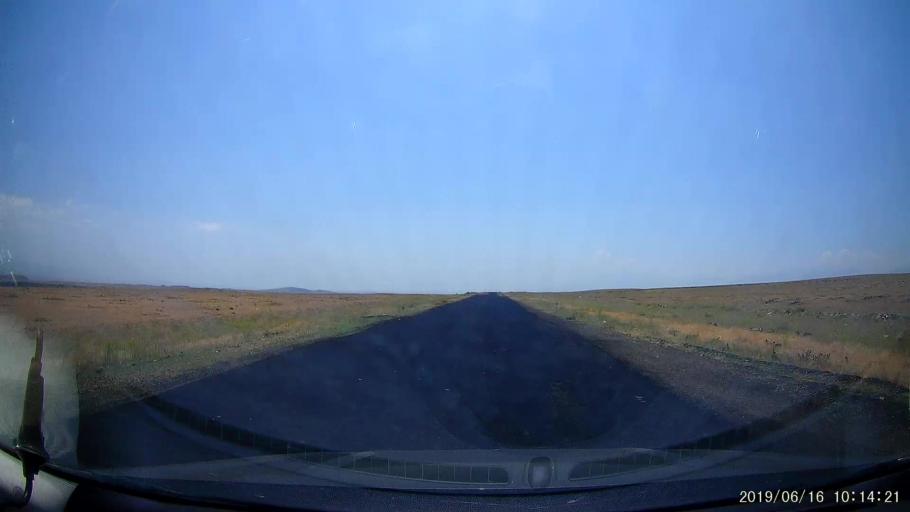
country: TR
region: Igdir
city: Tuzluca
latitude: 40.1856
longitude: 43.6611
